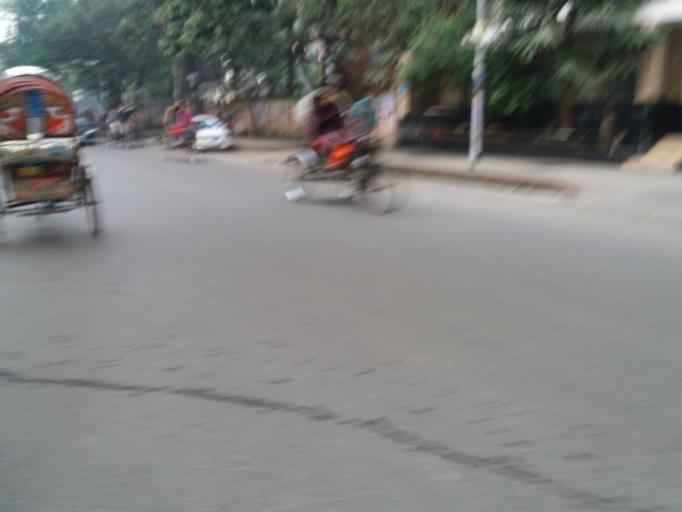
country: BD
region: Dhaka
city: Azimpur
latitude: 23.7436
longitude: 90.3798
